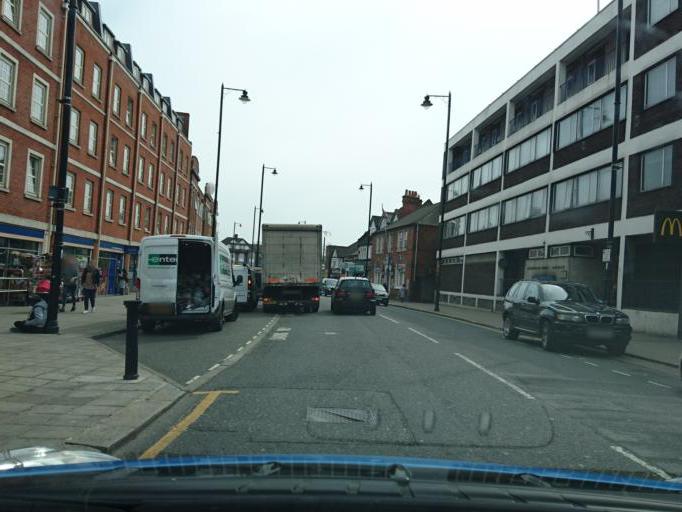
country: GB
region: England
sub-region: Greater London
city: Wood Green
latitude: 51.6330
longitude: -0.1296
